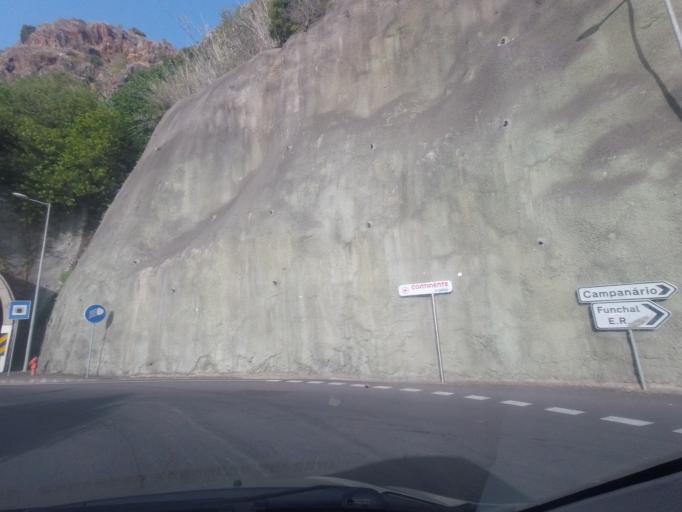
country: PT
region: Madeira
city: Ribeira Brava
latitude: 32.6725
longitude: -17.0624
